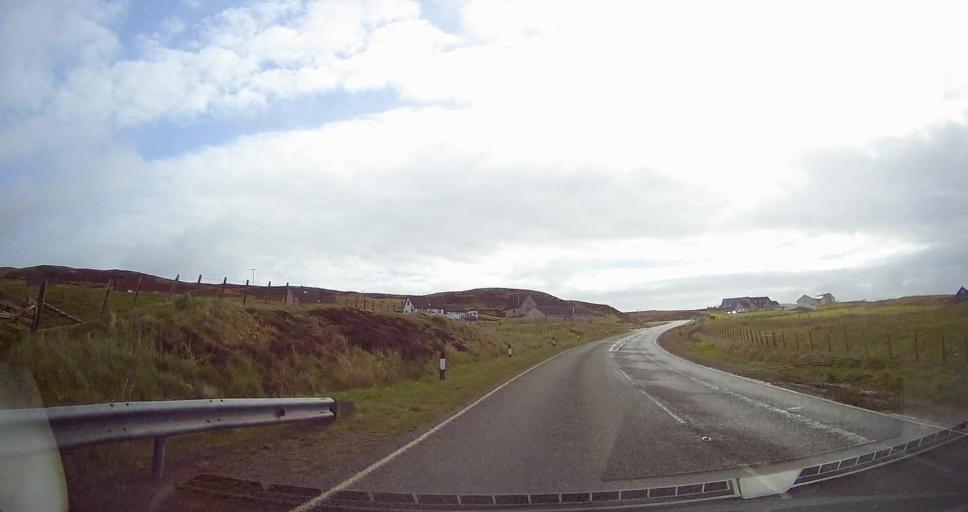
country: GB
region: Scotland
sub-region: Shetland Islands
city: Lerwick
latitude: 60.1046
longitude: -1.2286
